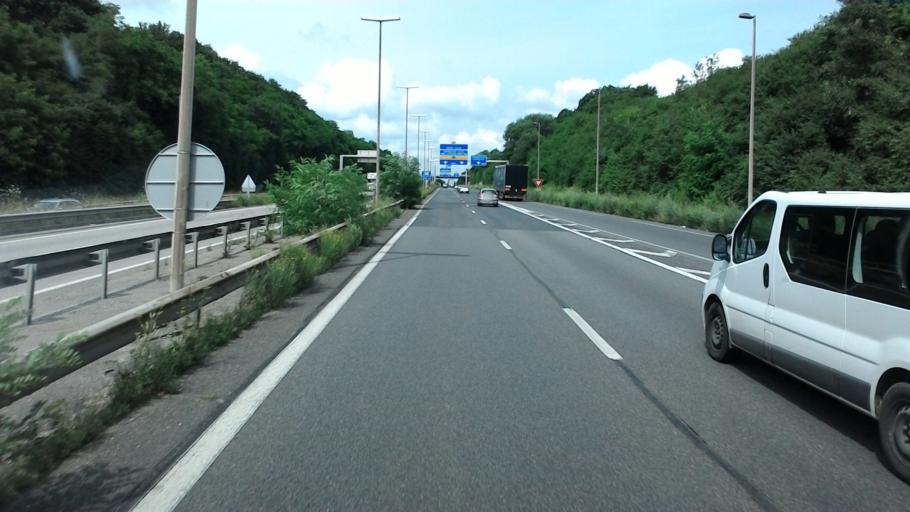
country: FR
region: Lorraine
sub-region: Departement de Meurthe-et-Moselle
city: Ludres
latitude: 48.6192
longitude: 6.1810
